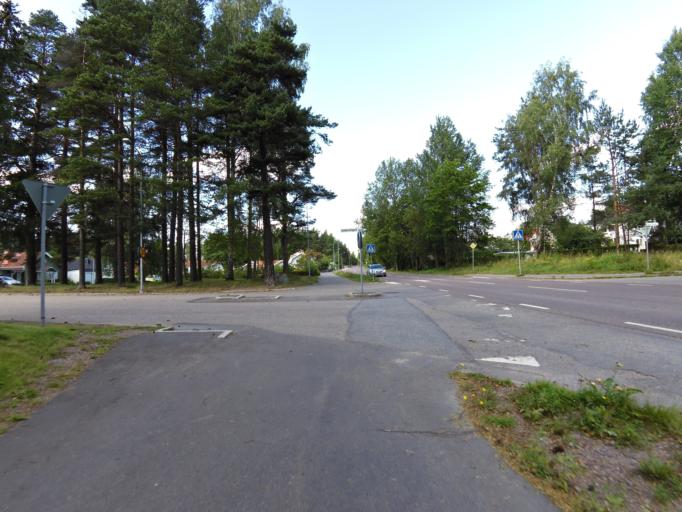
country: SE
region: Gaevleborg
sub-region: Gavle Kommun
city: Gavle
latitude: 60.7026
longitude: 17.1510
